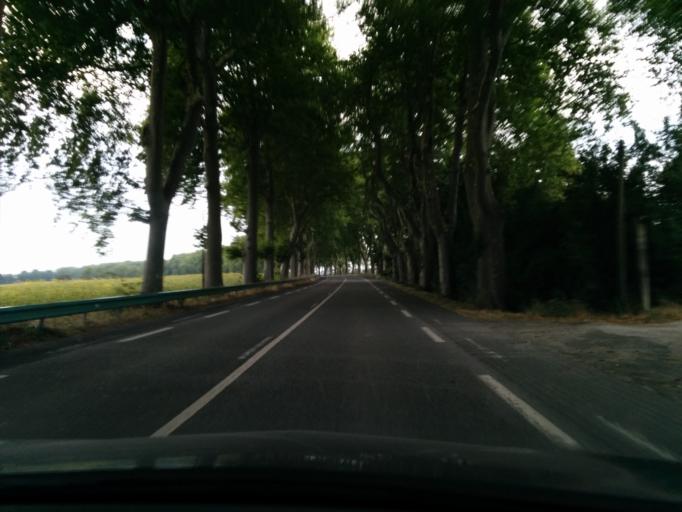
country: FR
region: Midi-Pyrenees
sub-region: Departement de la Haute-Garonne
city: Villefranche-de-Lauragais
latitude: 43.4101
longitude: 1.7055
